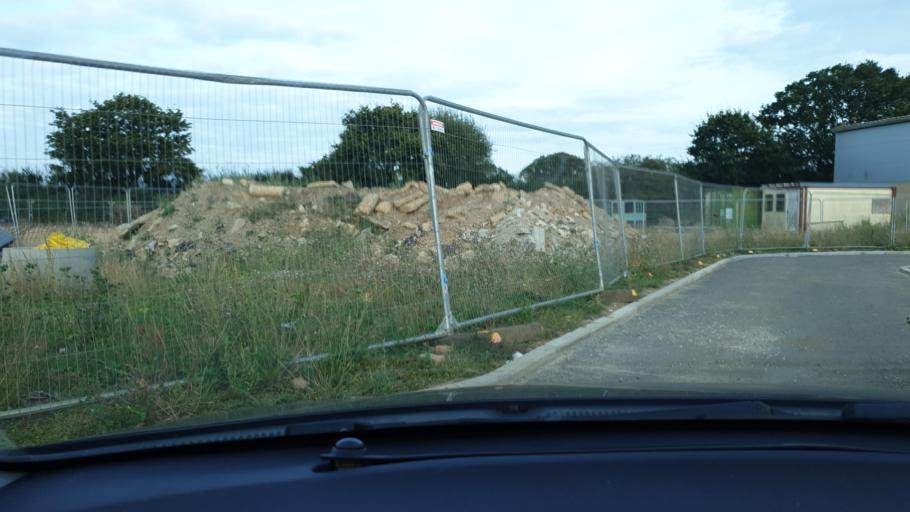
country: GB
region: England
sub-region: Essex
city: Little Clacton
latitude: 51.8214
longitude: 1.1670
